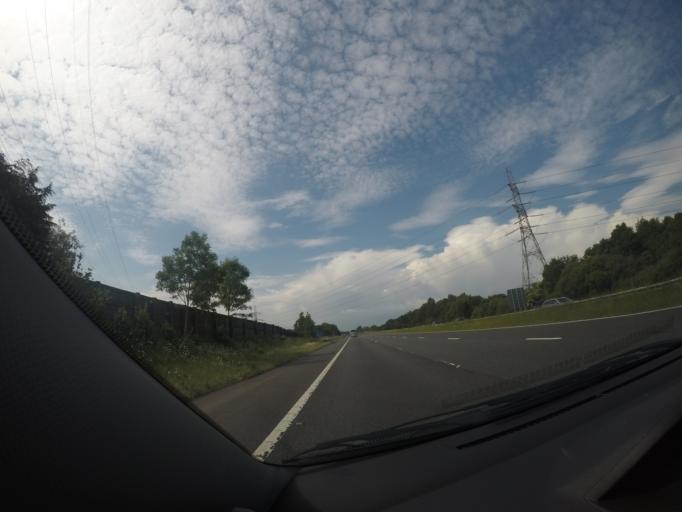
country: GB
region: England
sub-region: Cumbria
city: Carlisle
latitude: 54.9428
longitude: -2.9694
